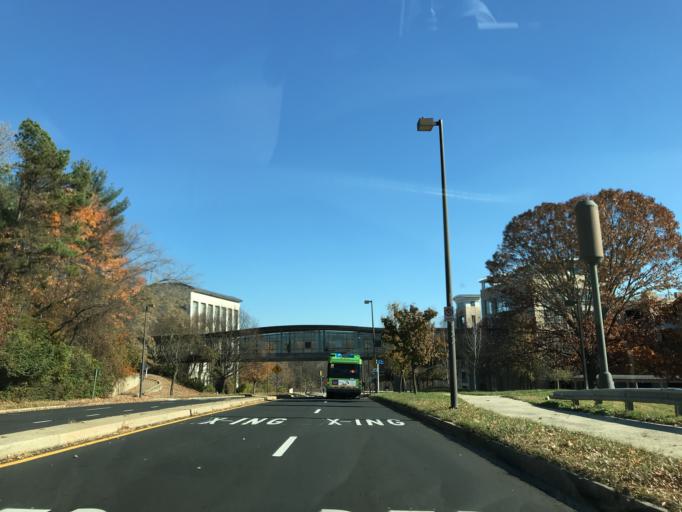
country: US
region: Maryland
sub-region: Montgomery County
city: North Bethesda
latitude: 39.0307
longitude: -77.1046
